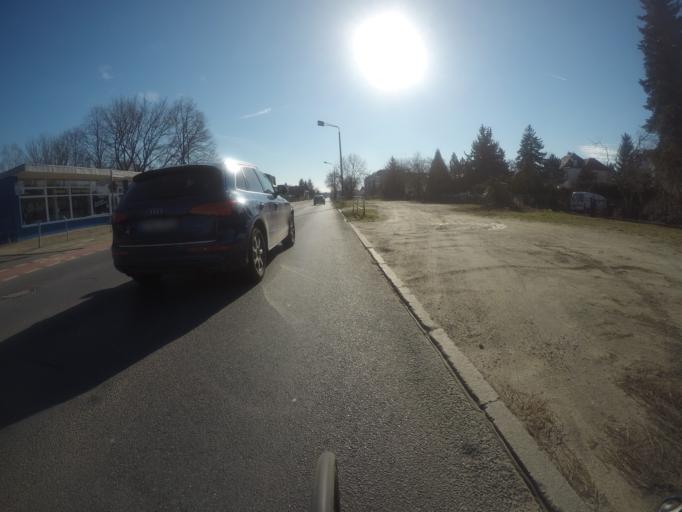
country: DE
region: Berlin
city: Kaulsdorf
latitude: 52.4940
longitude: 13.5765
